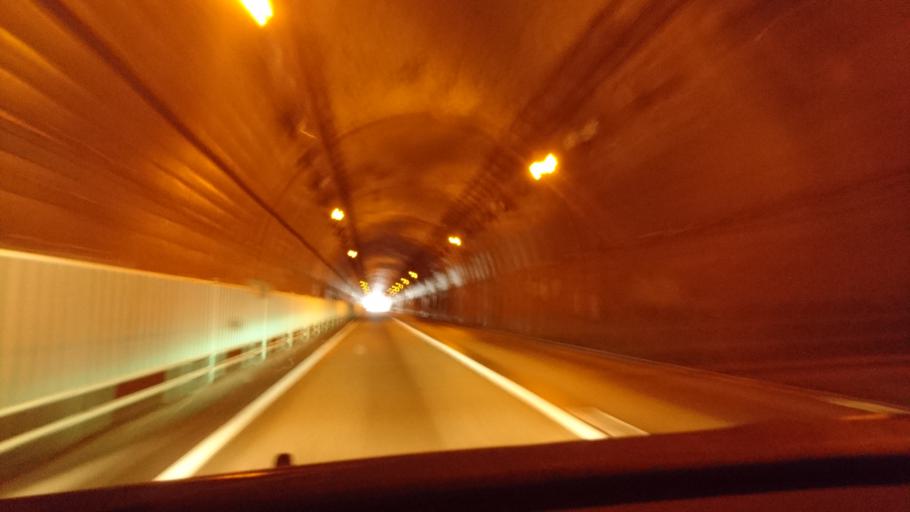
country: JP
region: Iwate
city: Kamaishi
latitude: 39.2092
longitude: 141.8726
